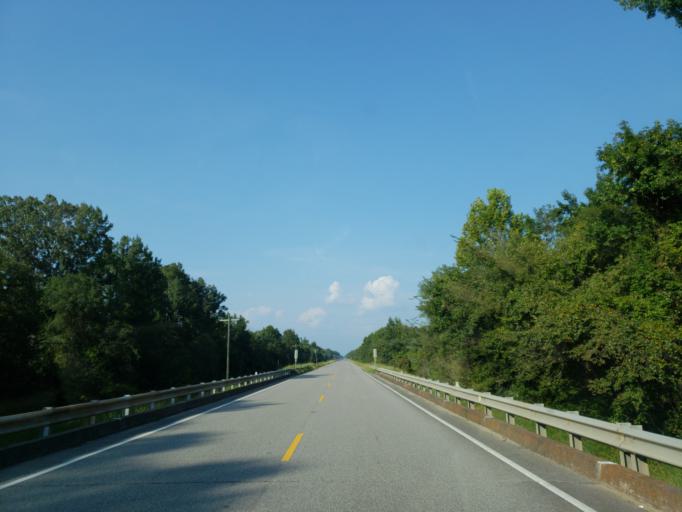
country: US
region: Alabama
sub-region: Sumter County
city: Livingston
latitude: 32.7129
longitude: -88.0784
